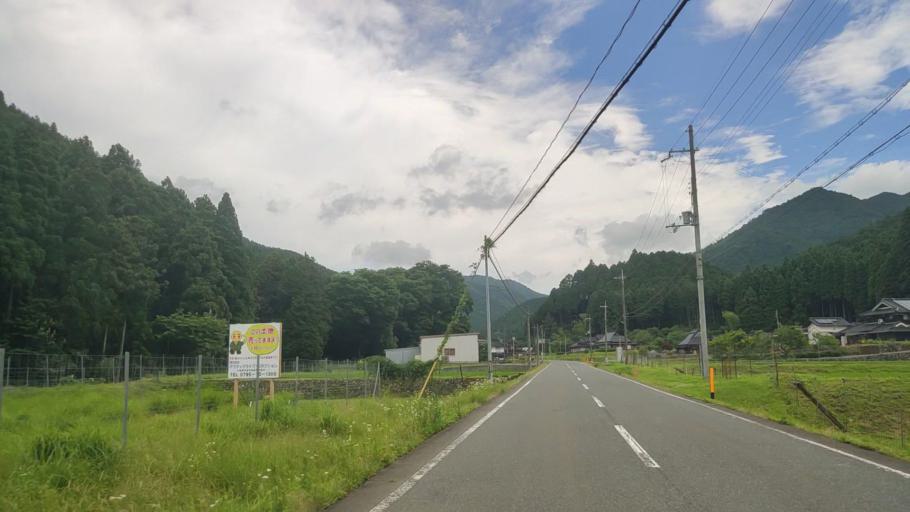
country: JP
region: Kyoto
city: Fukuchiyama
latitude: 35.1954
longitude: 134.9347
